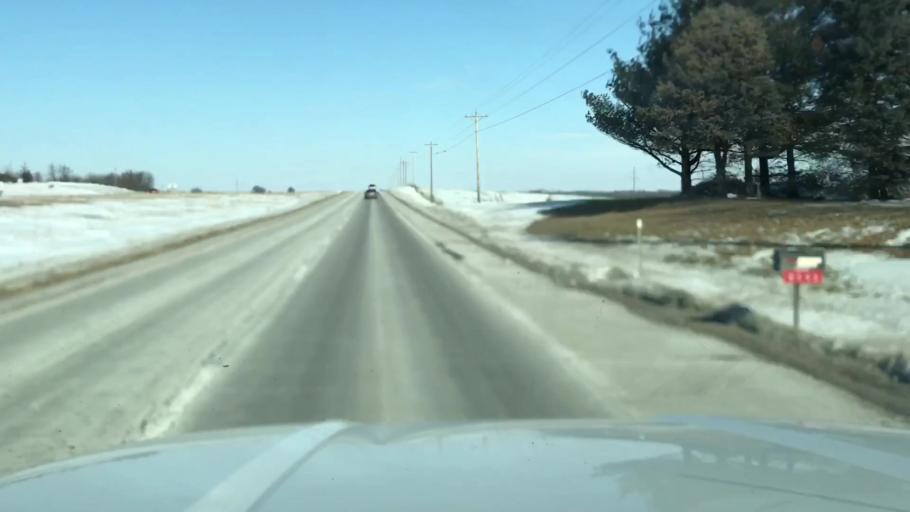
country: US
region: Missouri
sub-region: Andrew County
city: Savannah
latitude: 40.0020
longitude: -94.8797
